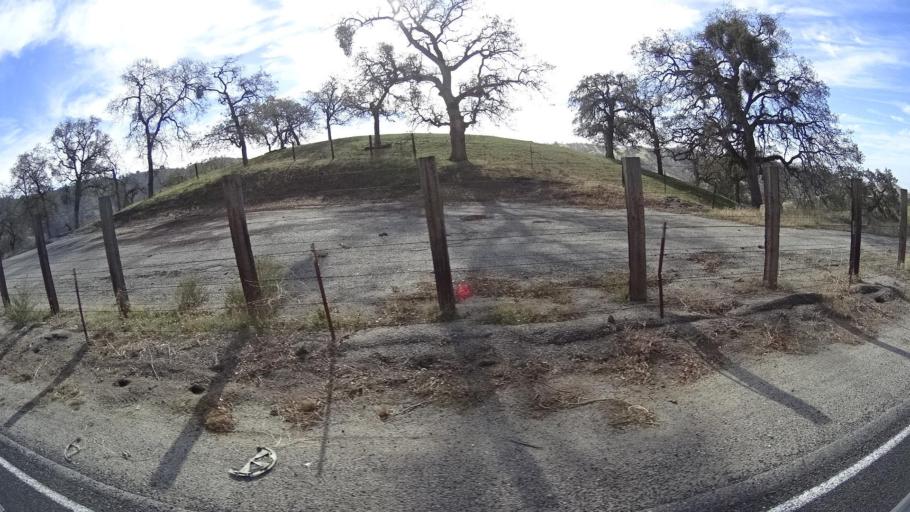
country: US
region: California
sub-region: Kern County
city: Alta Sierra
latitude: 35.6269
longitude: -118.8045
